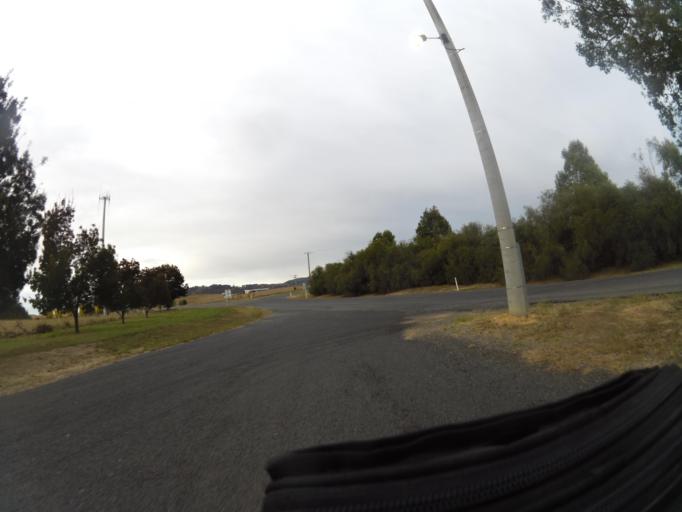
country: AU
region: New South Wales
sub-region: Greater Hume Shire
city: Holbrook
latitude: -36.0485
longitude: 147.9311
